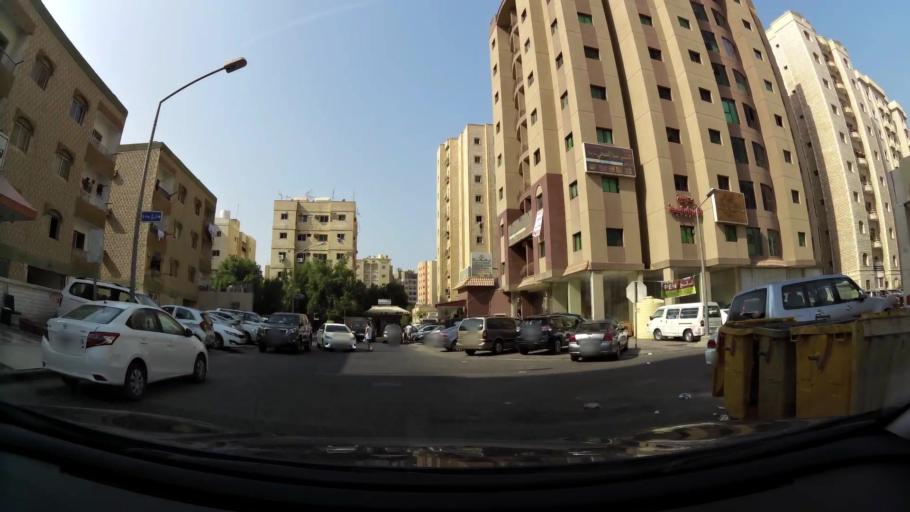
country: KW
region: Muhafazat Hawalli
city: Ar Rumaythiyah
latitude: 29.3201
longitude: 48.0586
